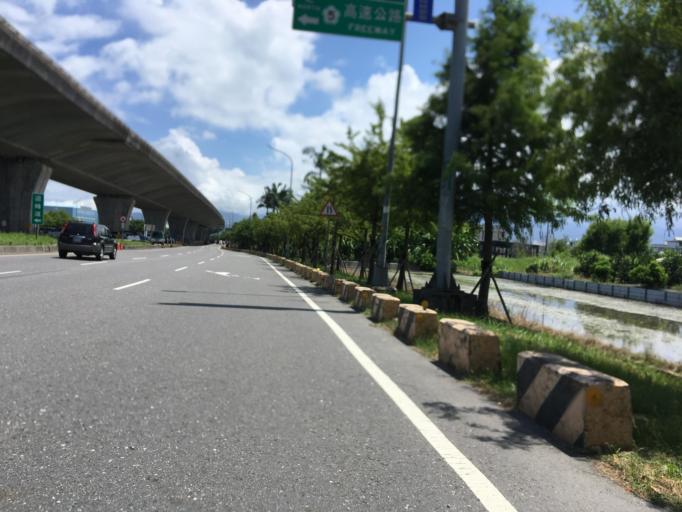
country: TW
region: Taiwan
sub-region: Yilan
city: Yilan
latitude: 24.6918
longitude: 121.7907
